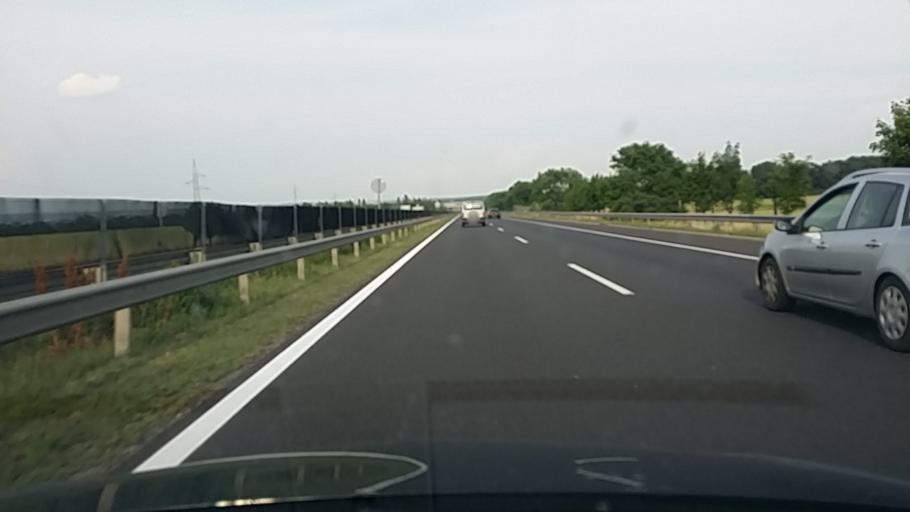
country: HU
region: Heves
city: Nagyrede
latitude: 47.7261
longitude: 19.8736
